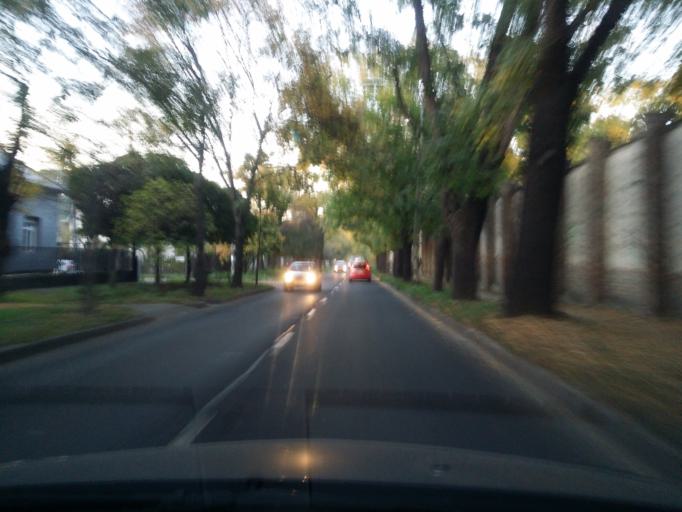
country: HU
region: Budapest
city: Budapest XV. keruelet
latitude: 47.5703
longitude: 19.1186
